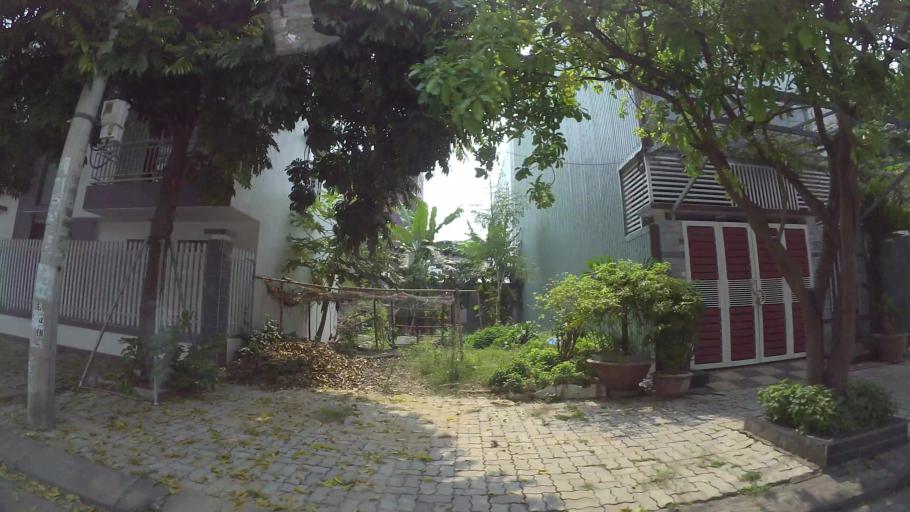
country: VN
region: Da Nang
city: Da Nang
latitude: 16.0863
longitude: 108.2325
